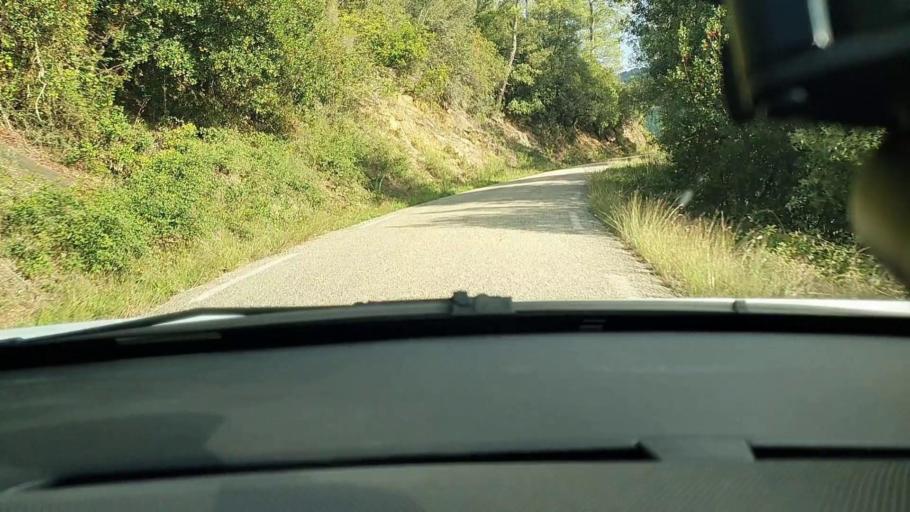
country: FR
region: Languedoc-Roussillon
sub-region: Departement du Gard
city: Besseges
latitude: 44.3197
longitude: 4.0450
